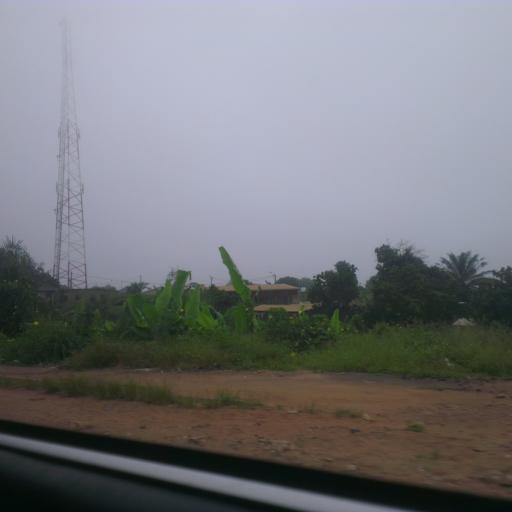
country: CI
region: Vallee du Bandama
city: Bouake
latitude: 7.6823
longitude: -5.0494
